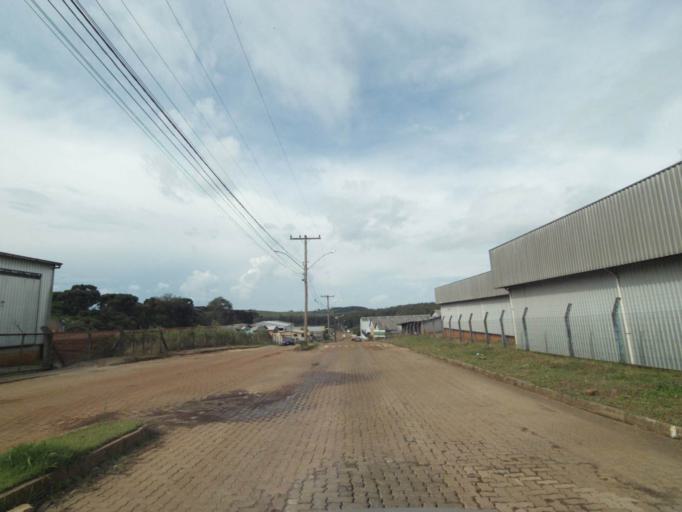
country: BR
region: Rio Grande do Sul
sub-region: Lagoa Vermelha
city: Lagoa Vermelha
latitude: -28.2295
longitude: -51.5137
